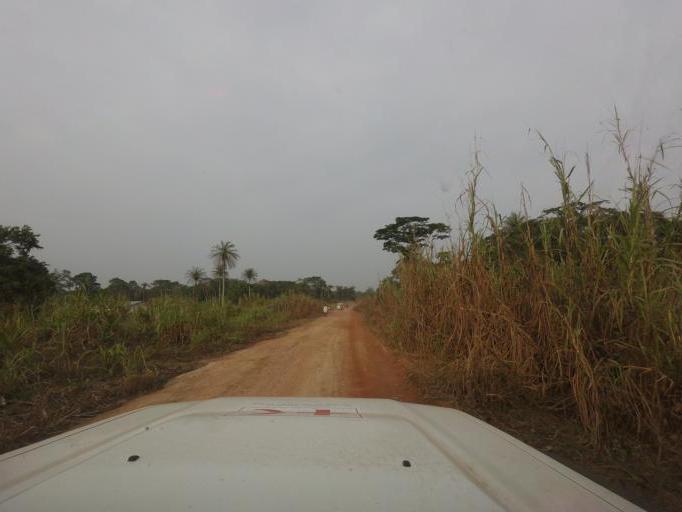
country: LR
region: Lofa
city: Voinjama
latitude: 8.3699
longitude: -9.9052
